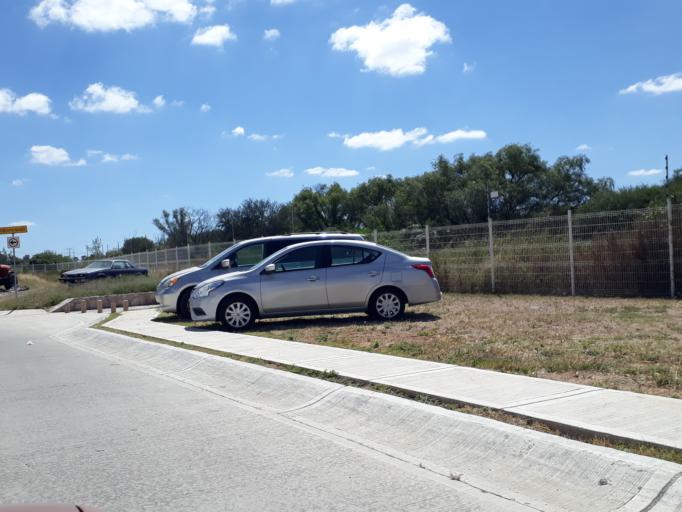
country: MX
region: Aguascalientes
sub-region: Aguascalientes
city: San Sebastian [Fraccionamiento]
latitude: 21.8292
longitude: -102.3022
